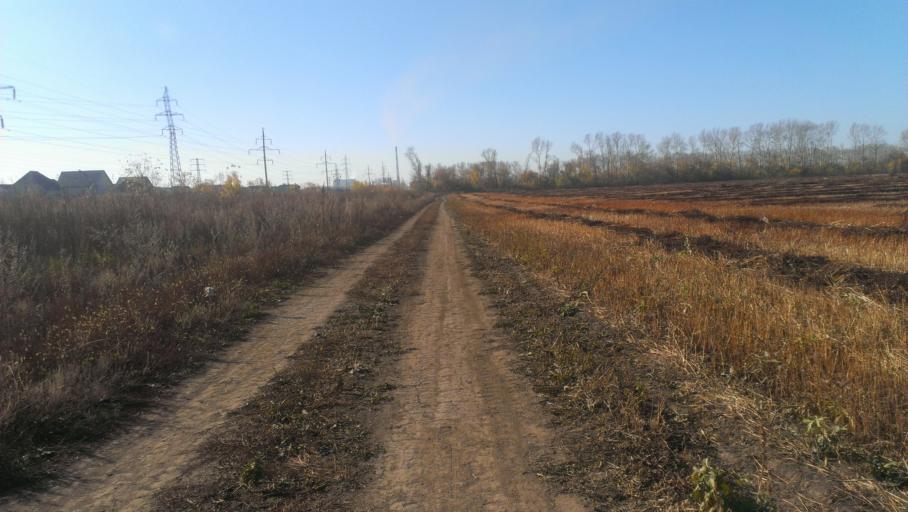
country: RU
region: Altai Krai
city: Novosilikatnyy
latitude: 53.3648
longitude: 83.6400
